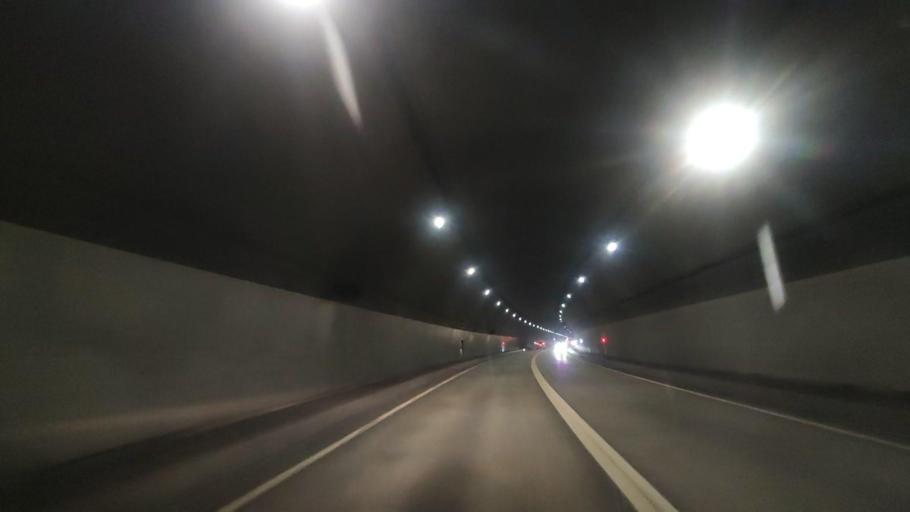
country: JP
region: Nagano
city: Okaya
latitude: 36.0938
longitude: 138.0811
